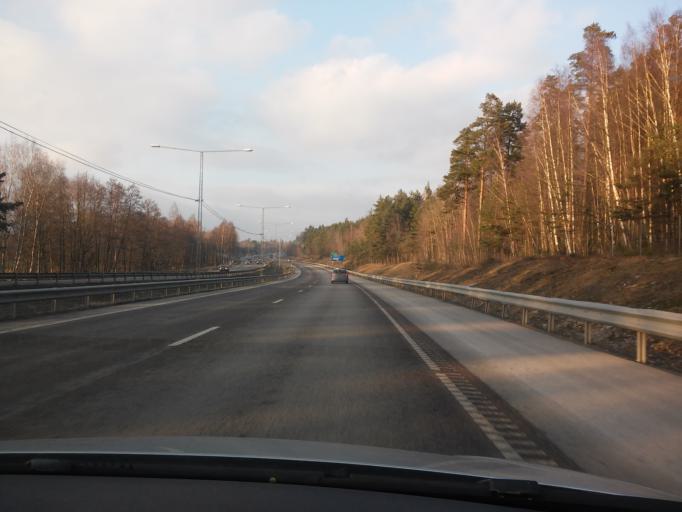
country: SE
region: Stockholm
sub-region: Vallentuna Kommun
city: Vallentuna
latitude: 59.4870
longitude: 18.1655
